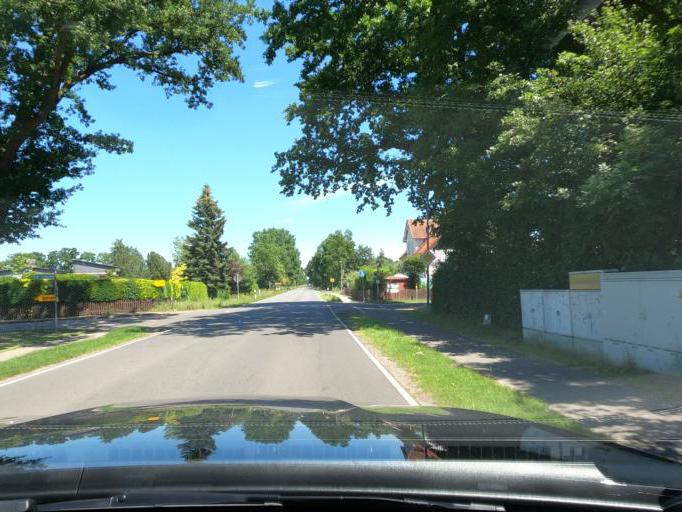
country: DE
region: Lower Saxony
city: Haenigsen
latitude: 52.4861
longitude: 10.1034
